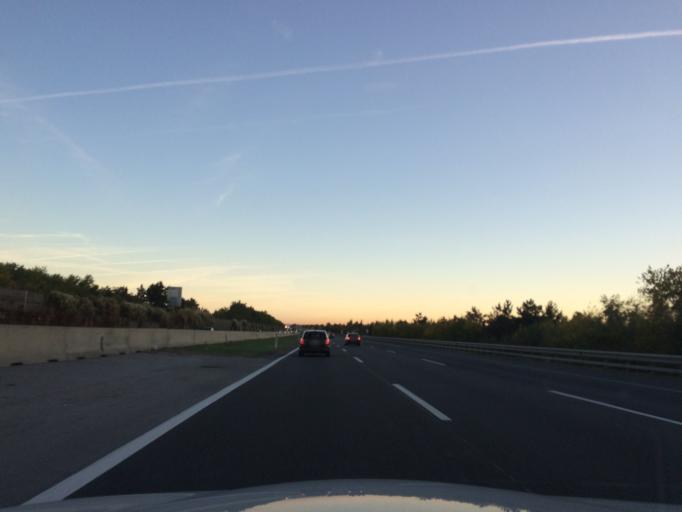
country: AT
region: Lower Austria
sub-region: Politischer Bezirk Baden
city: Leobersdorf
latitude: 47.9303
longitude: 16.2095
